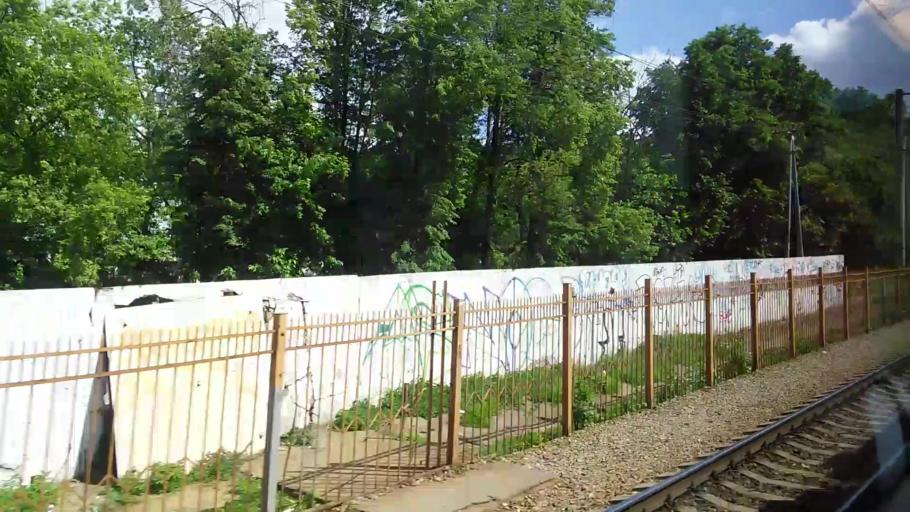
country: RU
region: Moscow
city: Novovladykino
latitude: 55.8179
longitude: 37.5773
